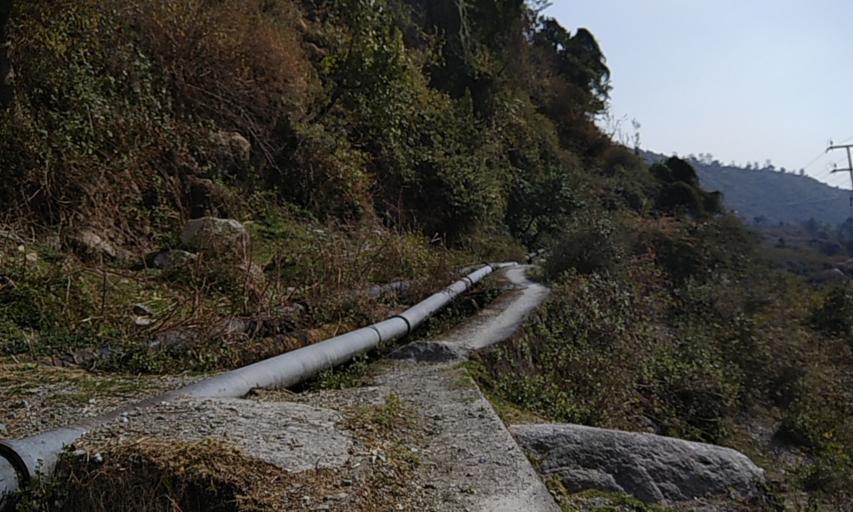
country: IN
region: Himachal Pradesh
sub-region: Kangra
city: Palampur
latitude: 32.1535
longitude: 76.5438
